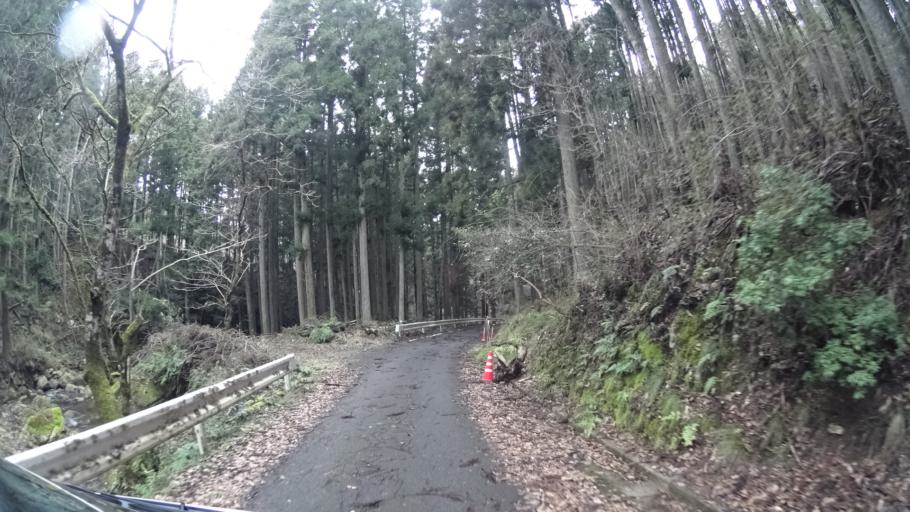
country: JP
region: Kyoto
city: Ayabe
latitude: 35.3153
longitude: 135.3691
